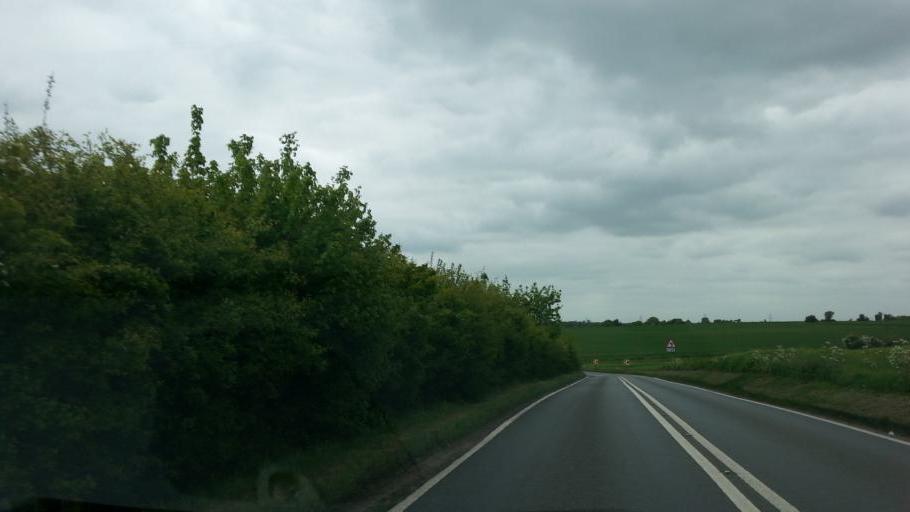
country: GB
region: England
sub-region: Suffolk
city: Bramford
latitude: 52.0532
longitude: 1.0749
